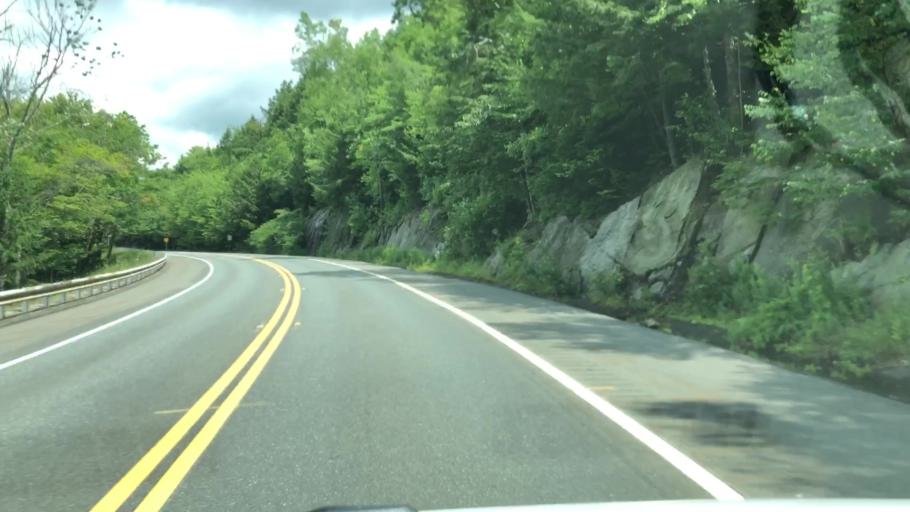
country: US
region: Massachusetts
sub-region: Hampshire County
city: Chesterfield
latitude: 42.4495
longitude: -72.8558
